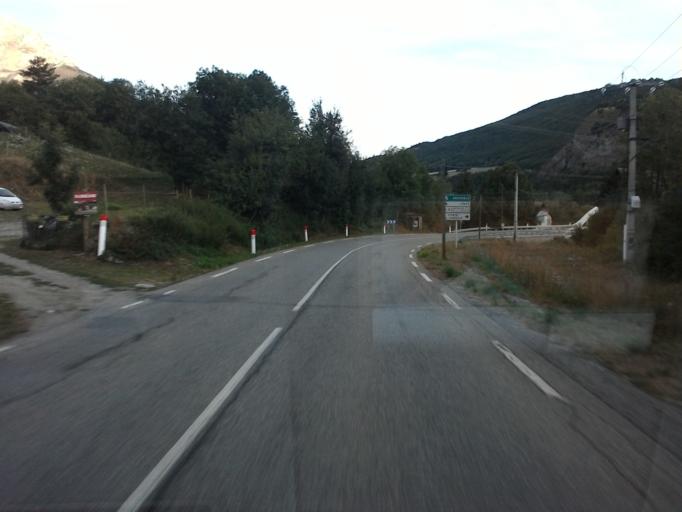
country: FR
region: Provence-Alpes-Cote d'Azur
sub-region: Departement des Hautes-Alpes
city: Saint-Bonnet-en-Champsaur
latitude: 44.7732
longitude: 6.0189
